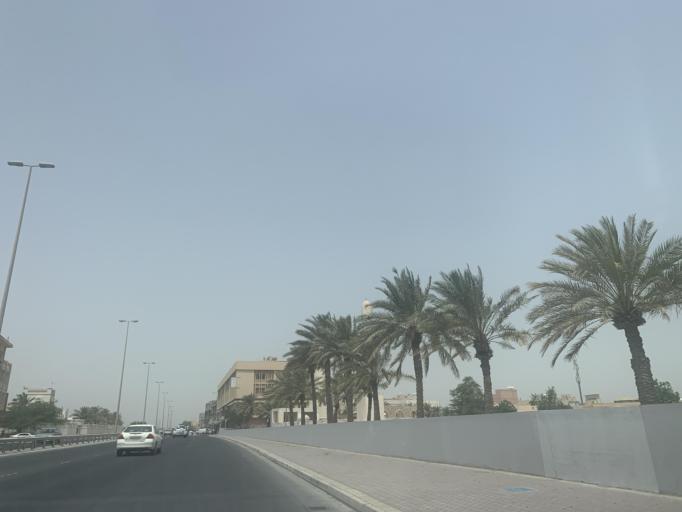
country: BH
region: Manama
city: Jidd Hafs
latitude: 26.2080
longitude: 50.5493
